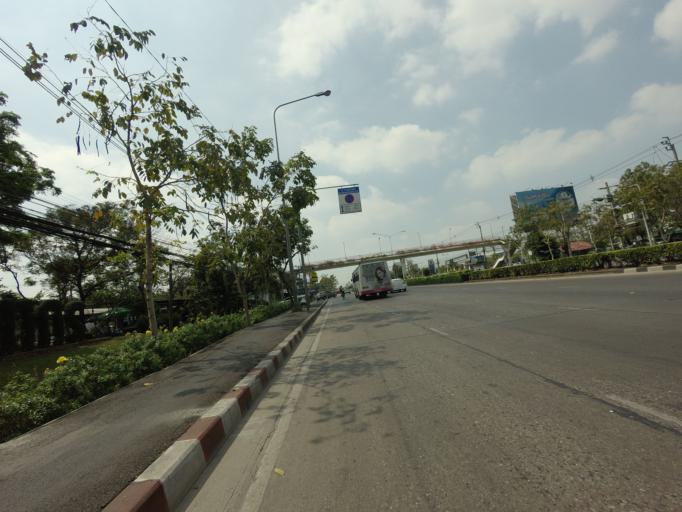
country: TH
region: Bangkok
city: Bueng Kum
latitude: 13.7779
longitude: 100.6755
